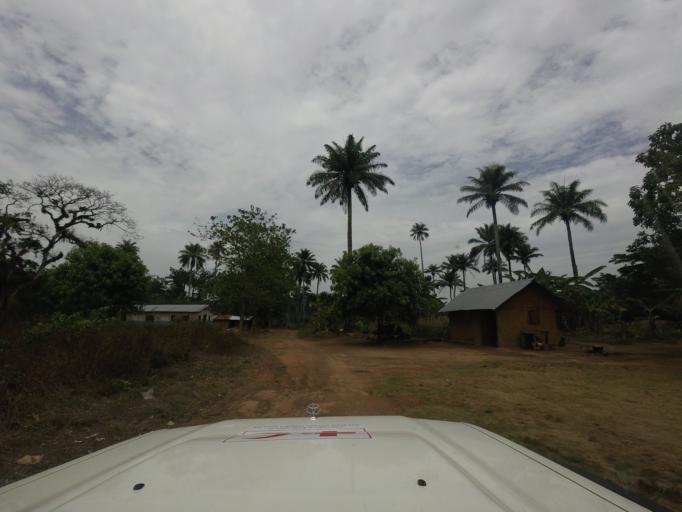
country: SL
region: Eastern Province
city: Buedu
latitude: 8.4218
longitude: -10.2647
